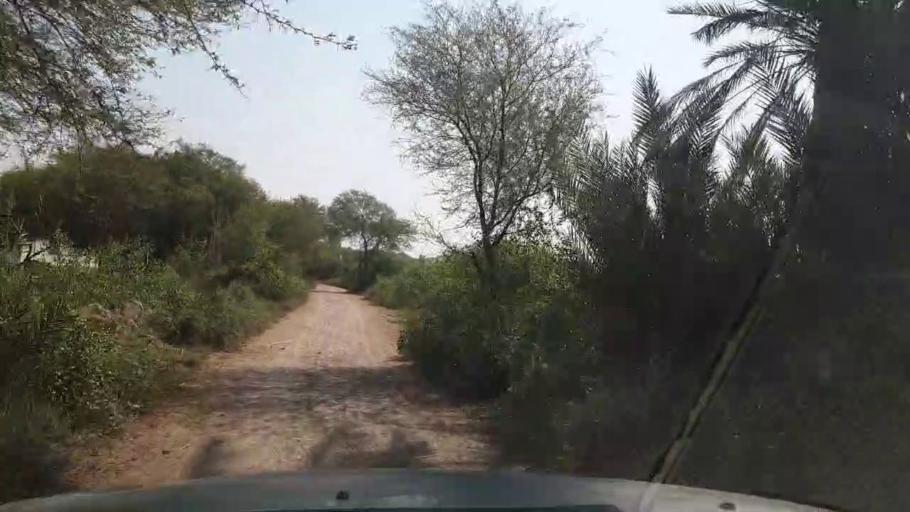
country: PK
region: Sindh
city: Bulri
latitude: 24.8827
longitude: 68.4025
